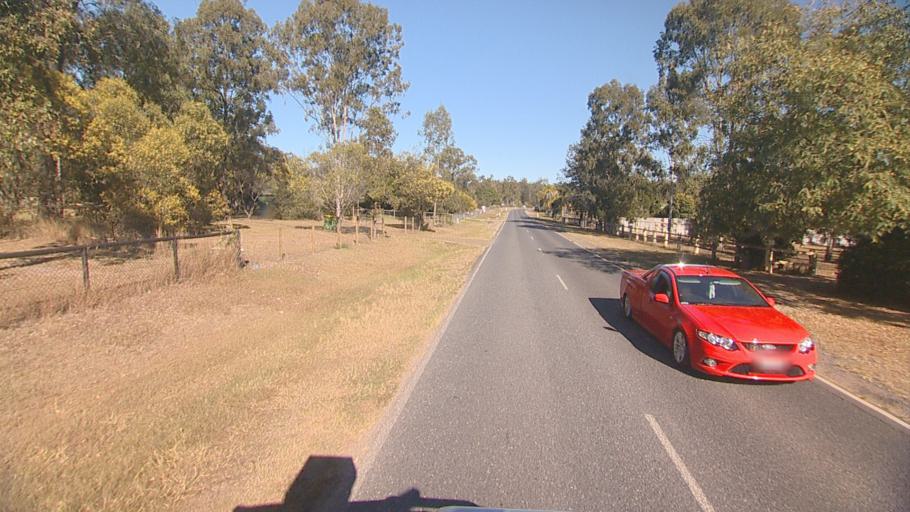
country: AU
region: Queensland
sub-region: Logan
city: North Maclean
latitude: -27.8181
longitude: 152.9641
